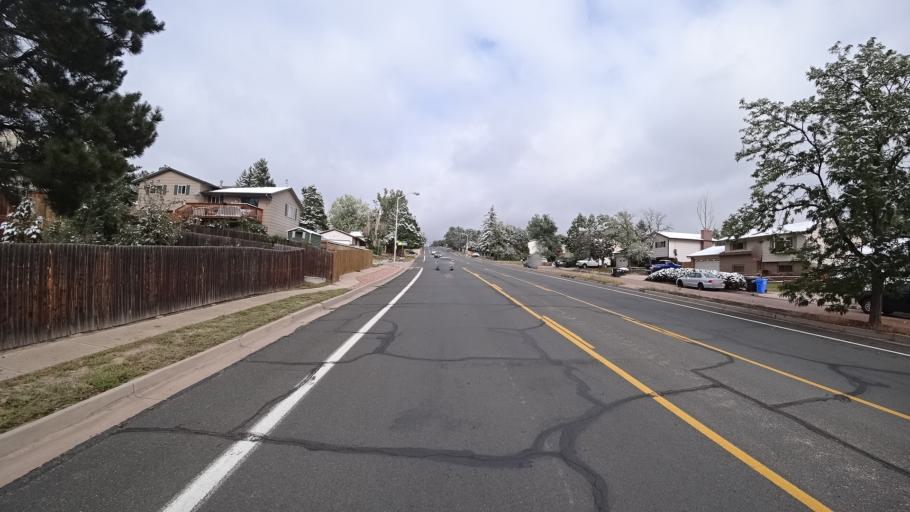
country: US
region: Colorado
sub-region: El Paso County
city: Cimarron Hills
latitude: 38.9146
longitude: -104.7694
